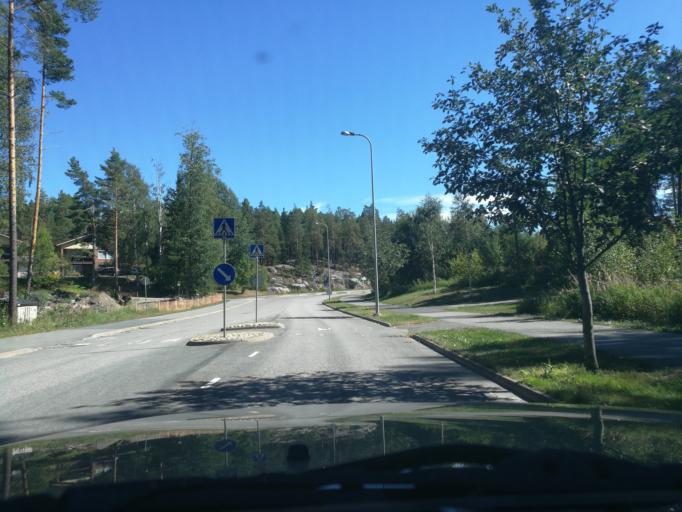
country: FI
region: Uusimaa
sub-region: Helsinki
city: Kerava
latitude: 60.3569
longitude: 25.1351
